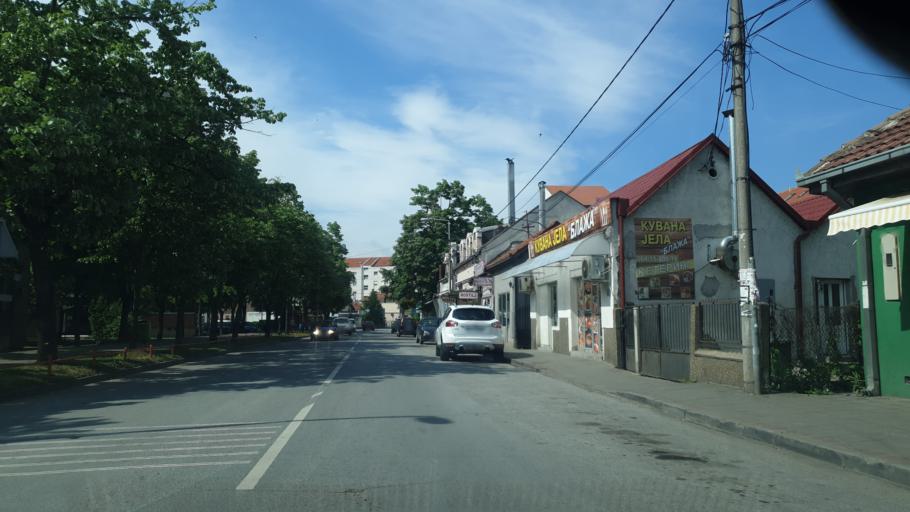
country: RS
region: Central Serbia
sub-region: Belgrade
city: Obrenovac
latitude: 44.6519
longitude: 20.1937
